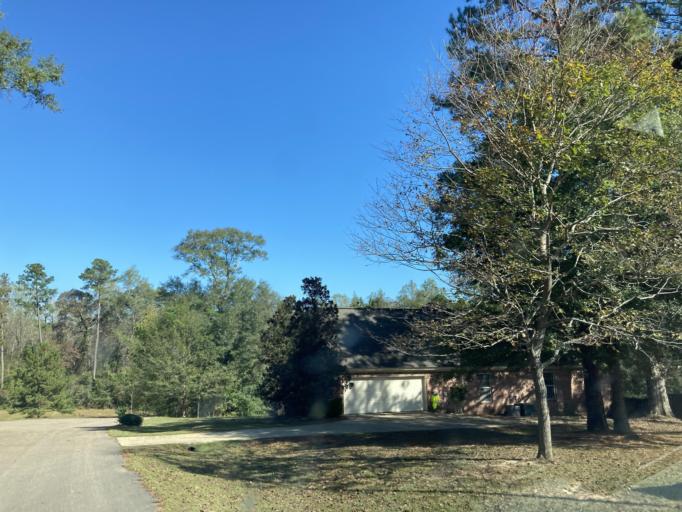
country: US
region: Mississippi
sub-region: Lamar County
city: Sumrall
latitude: 31.3490
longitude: -89.4957
